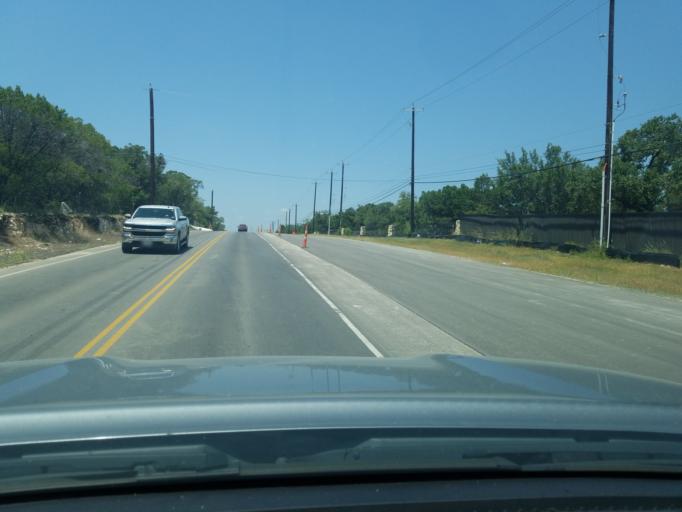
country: US
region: Texas
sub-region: Bexar County
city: Timberwood Park
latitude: 29.7081
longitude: -98.5071
